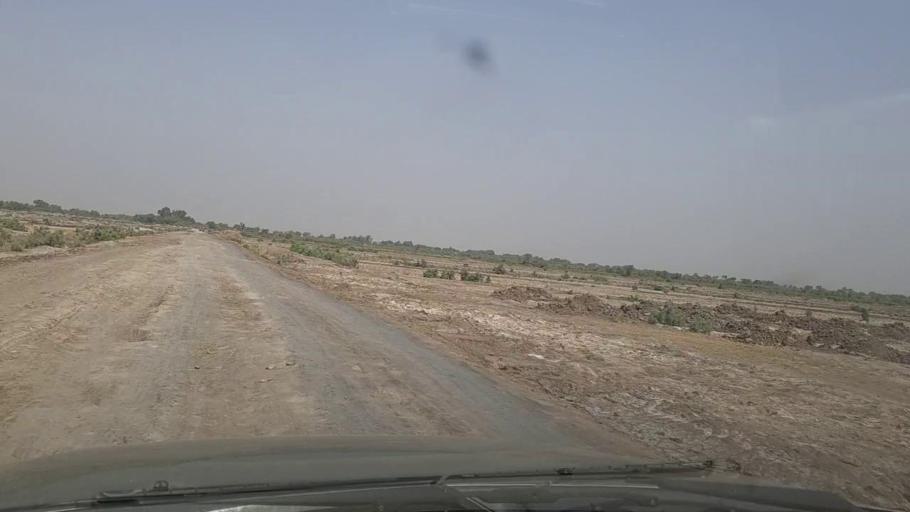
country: PK
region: Sindh
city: Thul
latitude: 28.3959
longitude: 68.7139
